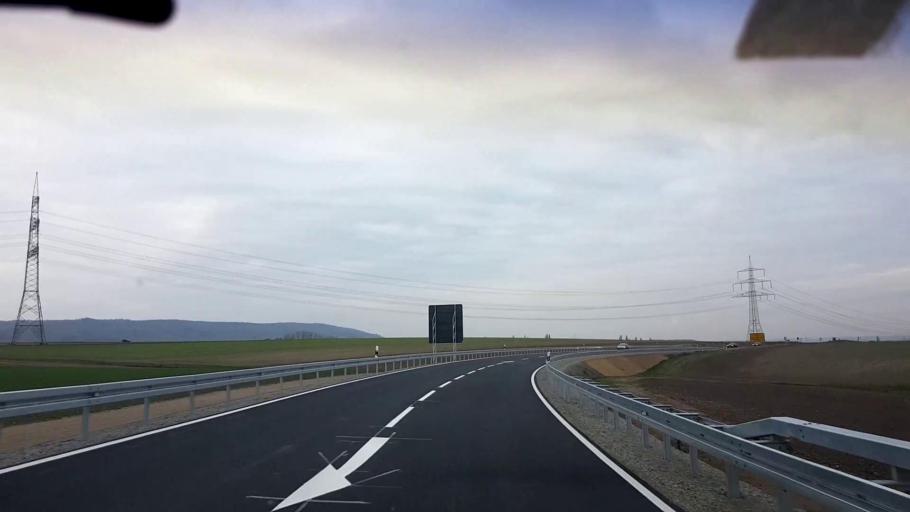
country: DE
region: Bavaria
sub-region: Regierungsbezirk Unterfranken
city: Castell
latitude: 49.7586
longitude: 10.3461
